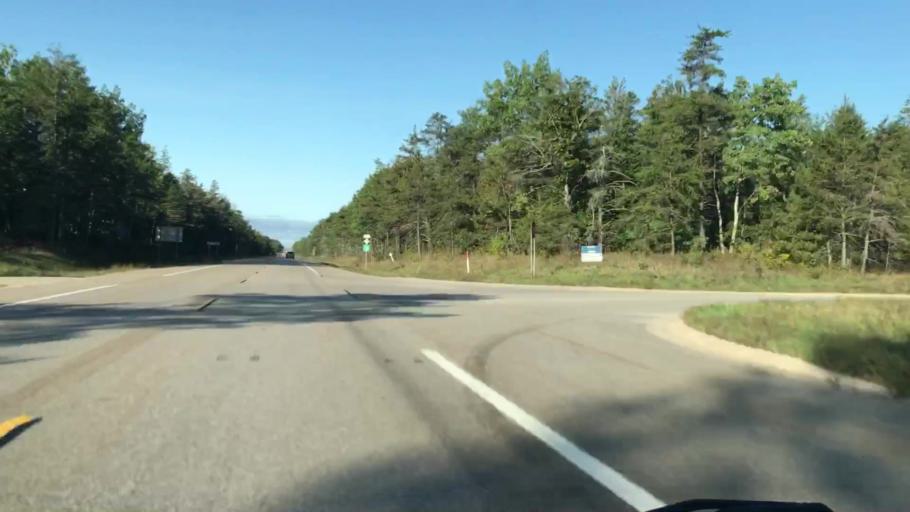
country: US
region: Michigan
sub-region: Chippewa County
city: Sault Ste. Marie
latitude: 46.3694
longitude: -84.7387
